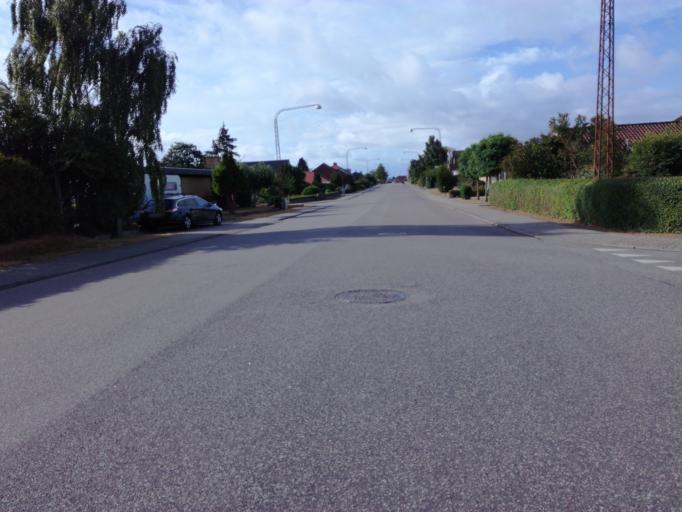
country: DK
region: South Denmark
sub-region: Fredericia Kommune
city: Fredericia
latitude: 55.5819
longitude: 9.7803
